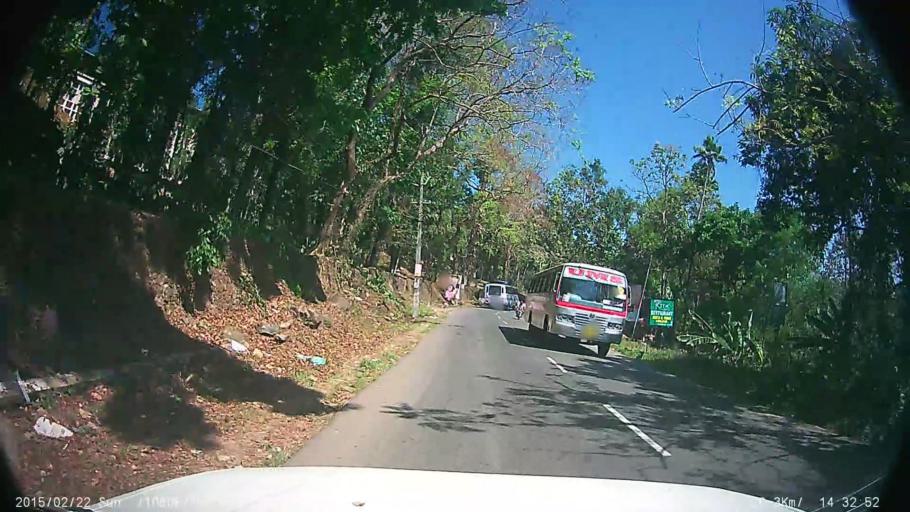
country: IN
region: Kerala
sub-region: Kottayam
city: Erattupetta
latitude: 9.5654
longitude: 76.7645
